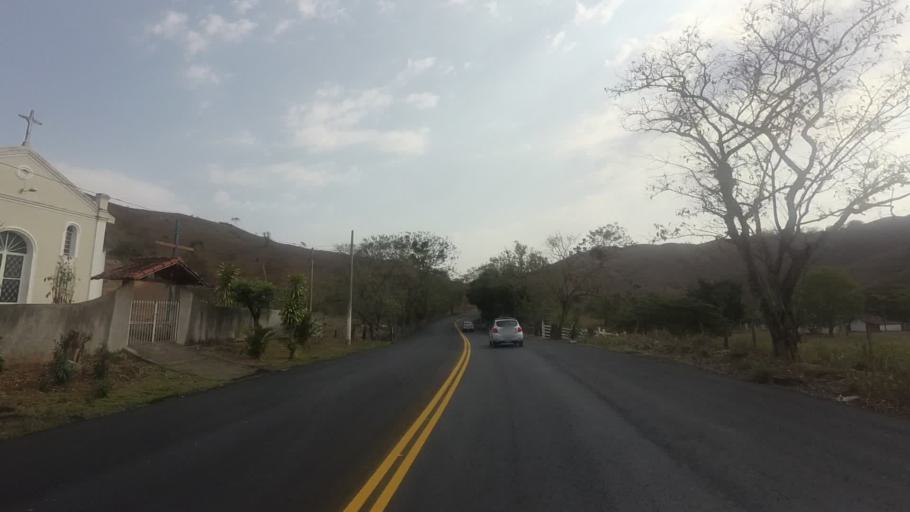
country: BR
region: Rio de Janeiro
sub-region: Bom Jesus Do Itabapoana
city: Bom Jesus do Itabapoana
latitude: -21.2130
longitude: -41.7336
